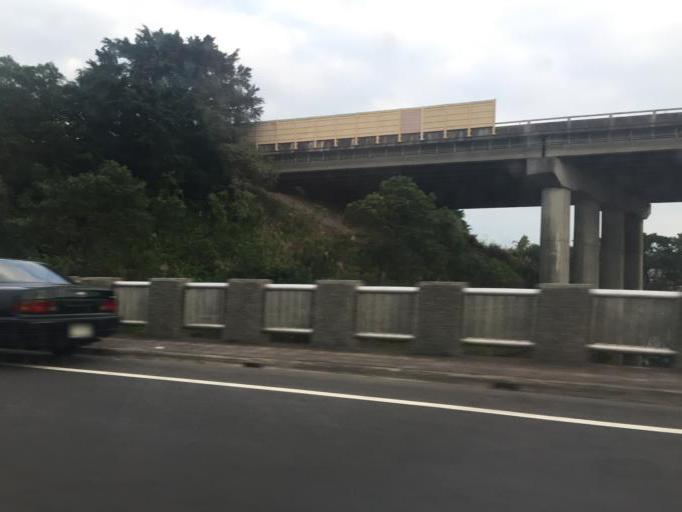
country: TW
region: Taiwan
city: Daxi
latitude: 24.8582
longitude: 121.2101
